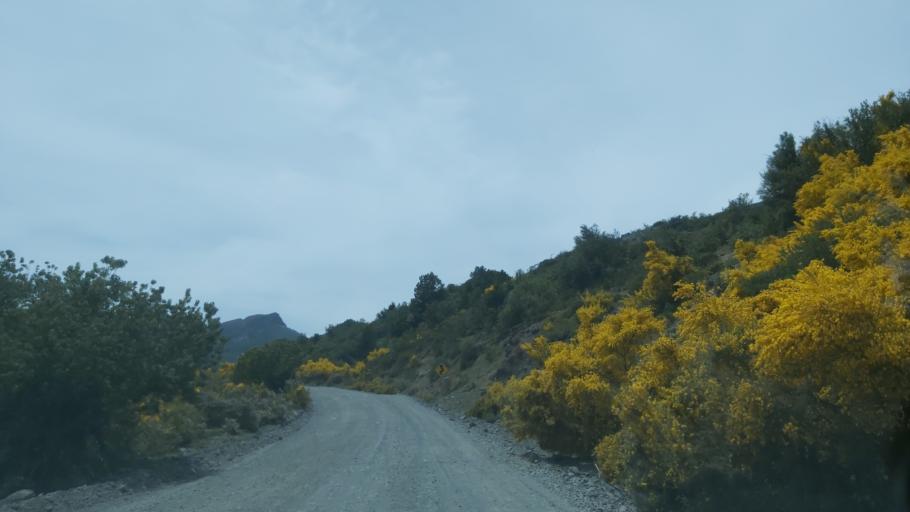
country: AR
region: Neuquen
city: Andacollo
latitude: -37.3930
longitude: -71.4057
